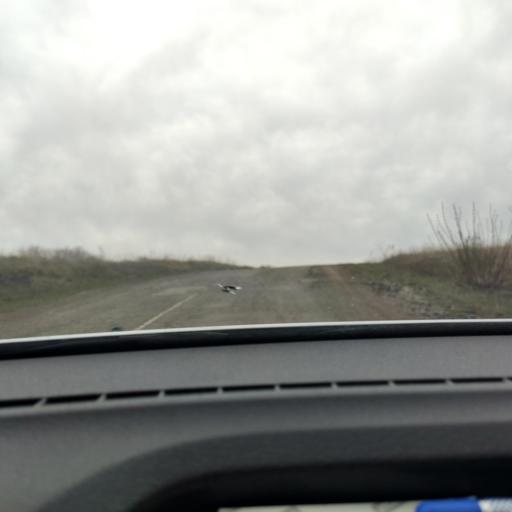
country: RU
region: Bashkortostan
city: Avdon
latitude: 54.6319
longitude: 55.6002
